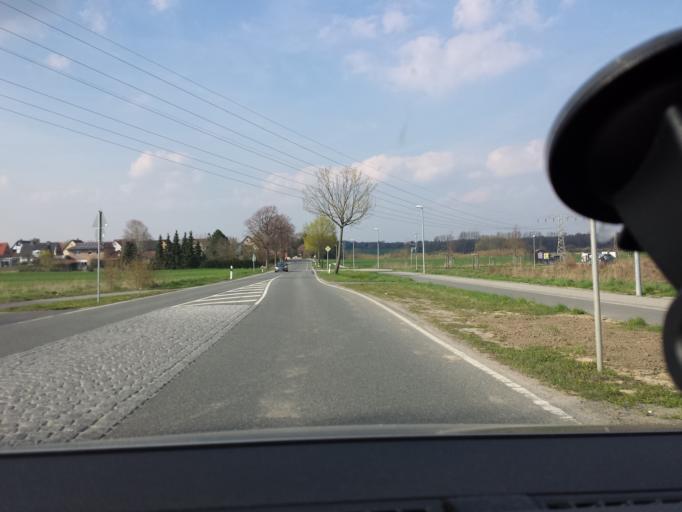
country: DE
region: Lower Saxony
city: Klein Schwulper
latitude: 52.2669
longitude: 10.4481
